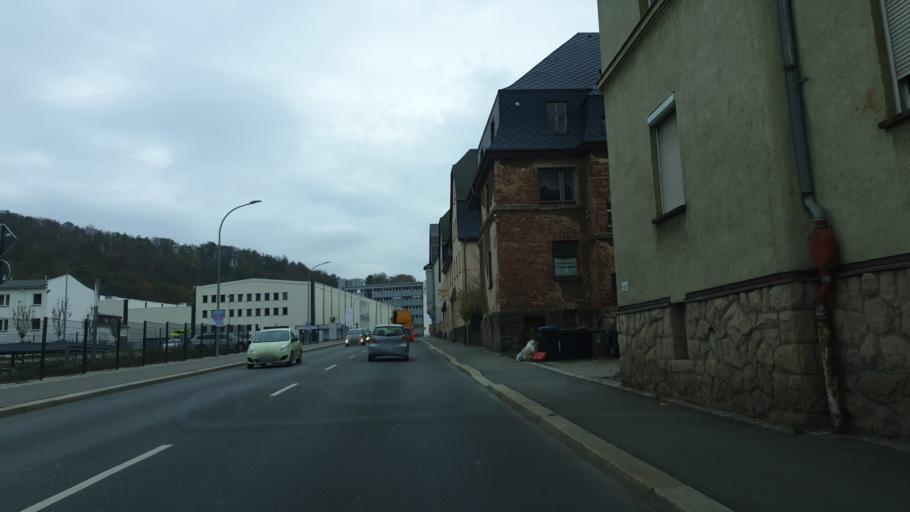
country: DE
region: Saxony
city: Schwarzenberg
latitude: 50.5468
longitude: 12.7879
